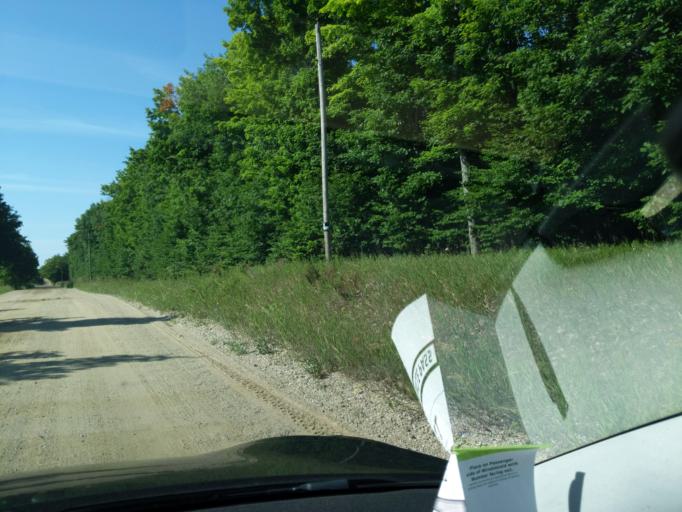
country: US
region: Michigan
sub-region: Mackinac County
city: Saint Ignace
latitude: 45.6926
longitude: -84.7123
